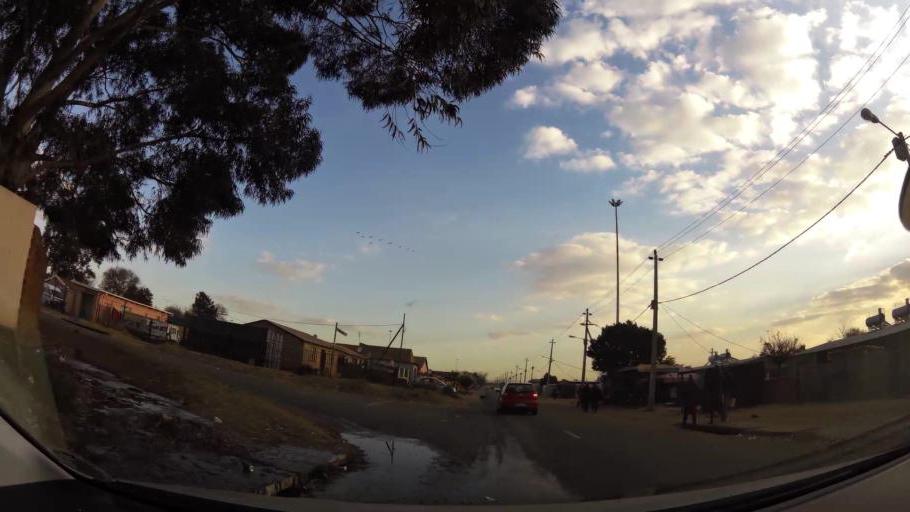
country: ZA
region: Gauteng
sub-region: City of Johannesburg Metropolitan Municipality
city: Soweto
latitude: -26.2636
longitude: 27.8982
